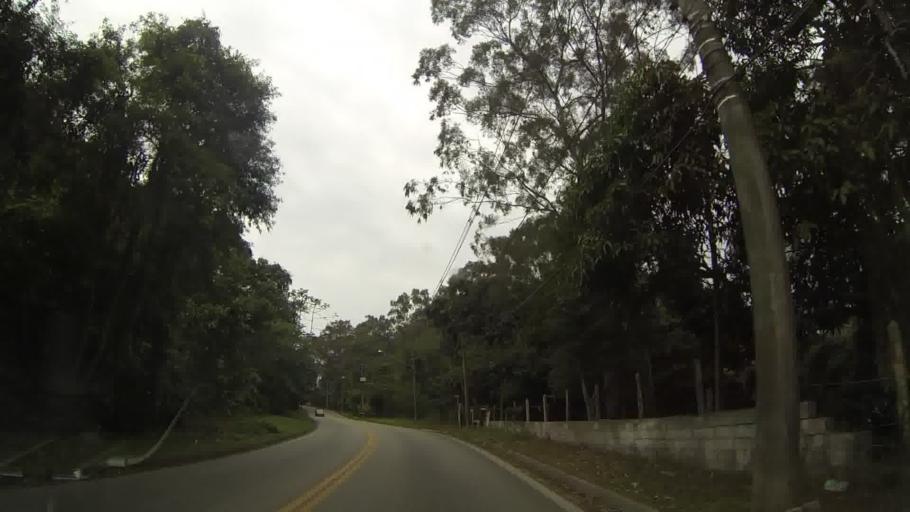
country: BR
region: Sao Paulo
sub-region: Sao Sebastiao
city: Sao Sebastiao
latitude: -23.8259
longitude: -45.4267
